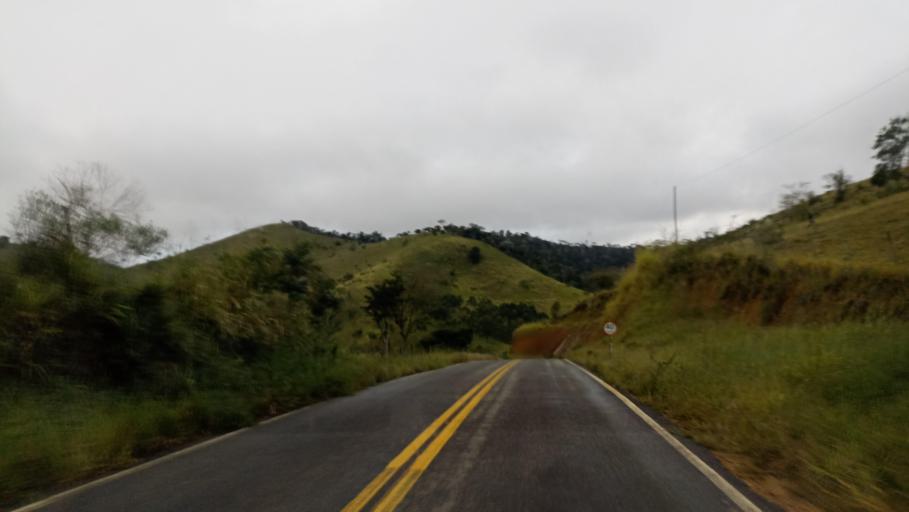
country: BR
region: Bahia
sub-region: Itanhem
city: Itanhem
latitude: -16.6910
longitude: -40.5127
